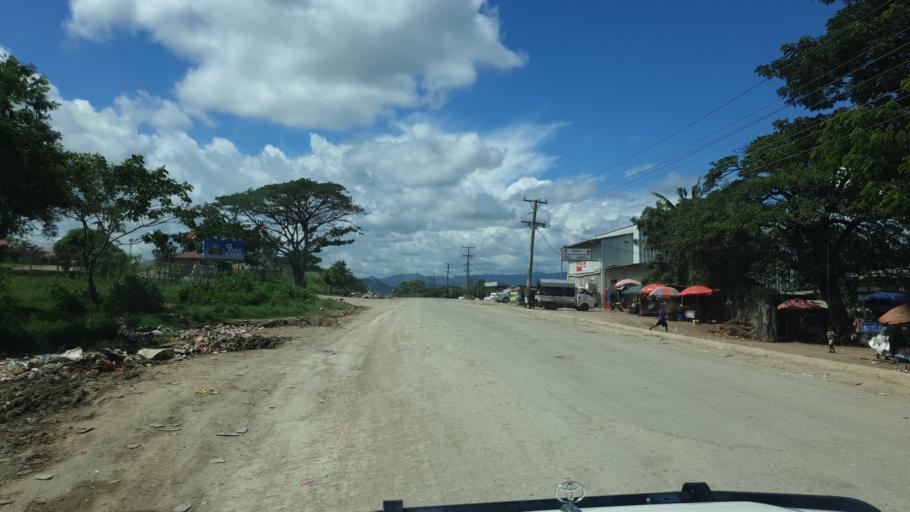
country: PG
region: National Capital
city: Port Moresby
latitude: -9.4049
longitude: 147.2276
